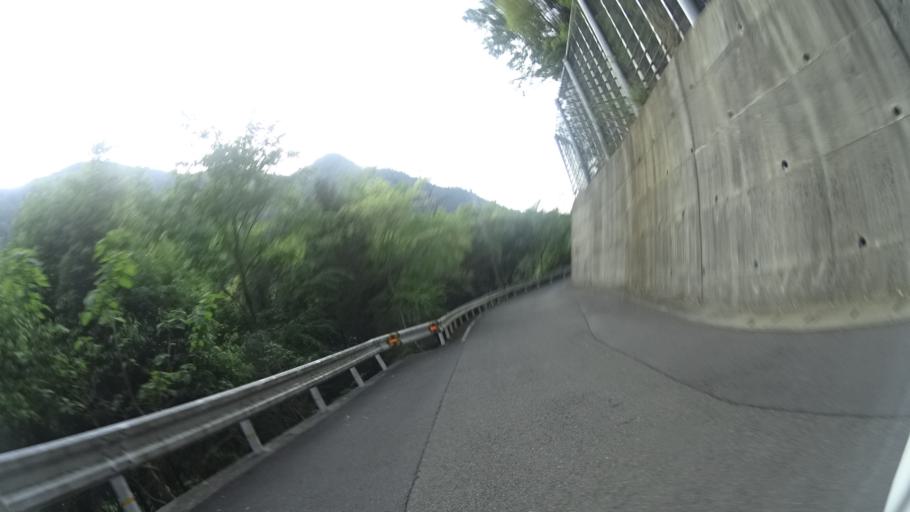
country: JP
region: Tokushima
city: Ikedacho
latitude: 33.9325
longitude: 133.8176
